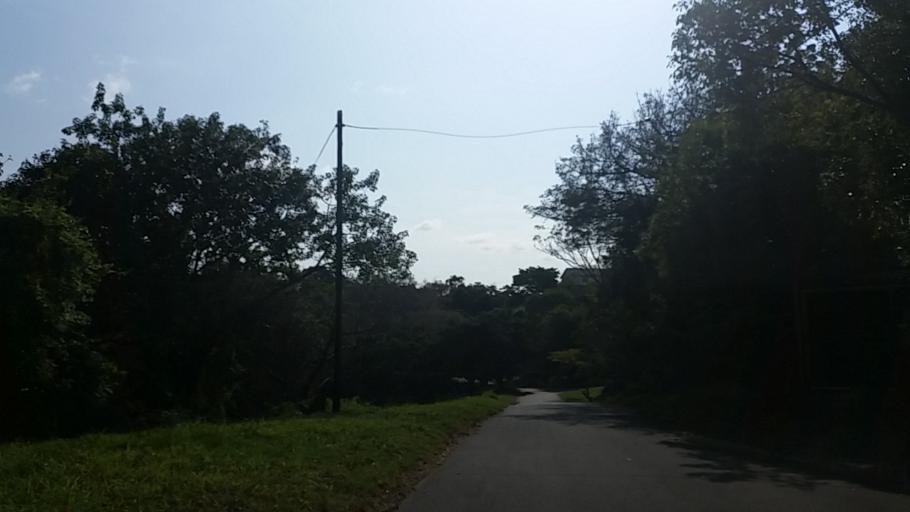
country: ZA
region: KwaZulu-Natal
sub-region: eThekwini Metropolitan Municipality
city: Berea
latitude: -29.8336
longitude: 30.9545
